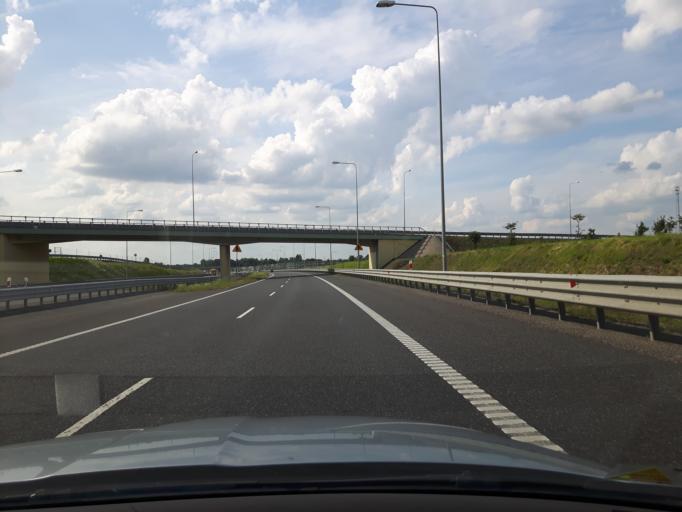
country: PL
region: Warmian-Masurian Voivodeship
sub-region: Powiat olsztynski
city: Olsztynek
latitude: 53.5824
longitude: 20.2529
